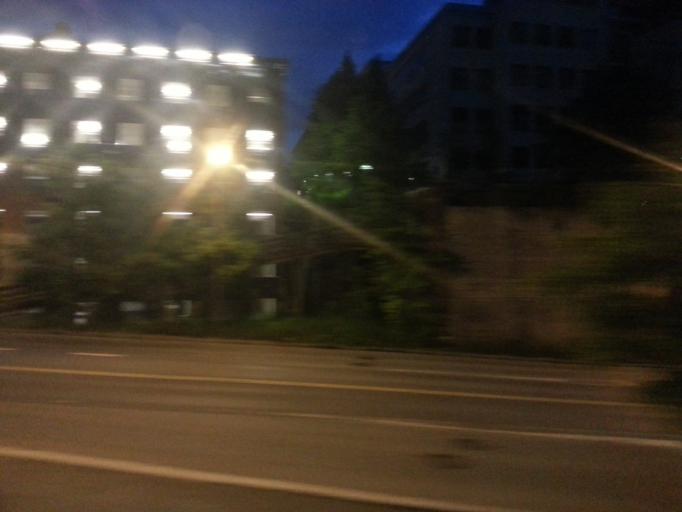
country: NO
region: Oppland
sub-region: Lillehammer
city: Lillehammer
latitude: 61.1166
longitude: 10.4610
